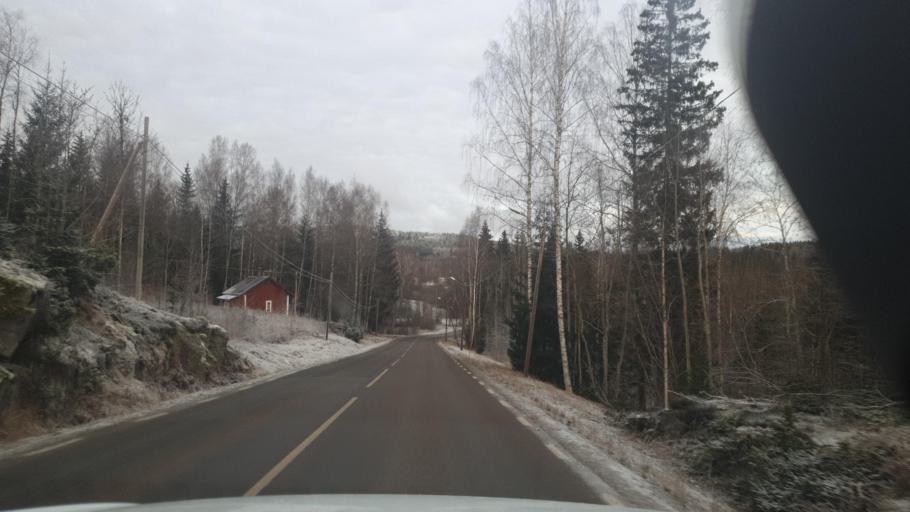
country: SE
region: Vaermland
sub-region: Eda Kommun
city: Amotfors
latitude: 59.6721
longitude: 12.4185
